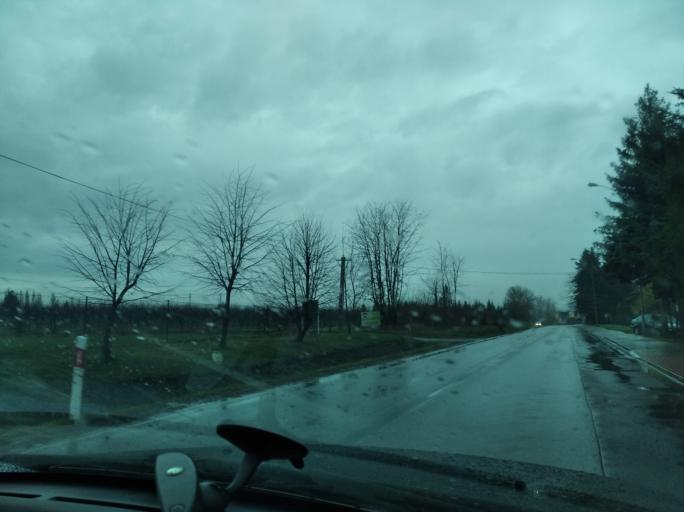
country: PL
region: Subcarpathian Voivodeship
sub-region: Powiat lancucki
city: Albigowa
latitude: 50.0275
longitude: 22.2266
